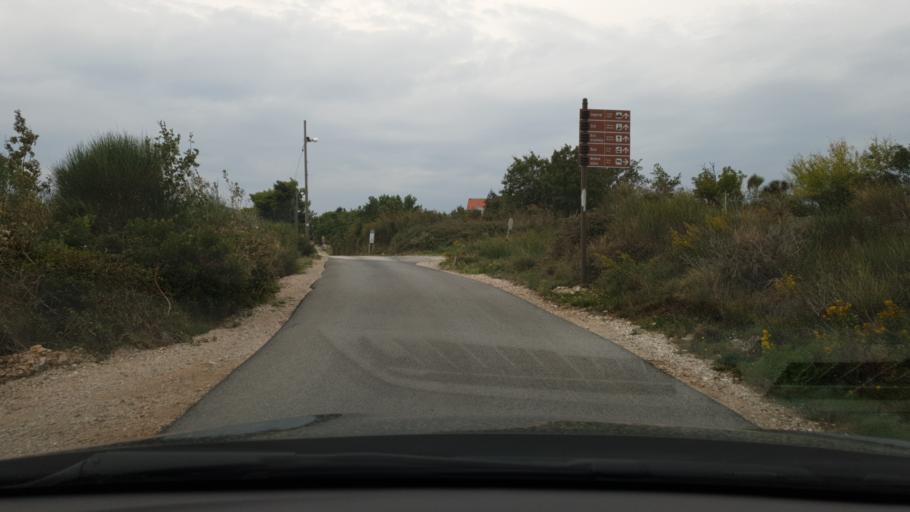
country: HR
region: Dubrovacko-Neretvanska
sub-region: Grad Dubrovnik
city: Dubrovnik
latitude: 42.6408
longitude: 18.1308
